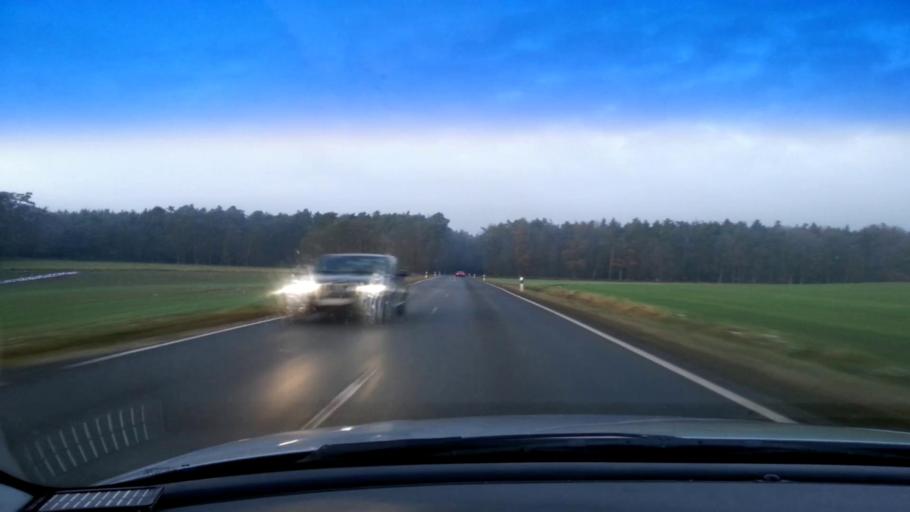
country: DE
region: Bavaria
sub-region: Upper Franconia
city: Pommersfelden
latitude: 49.7963
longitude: 10.8271
